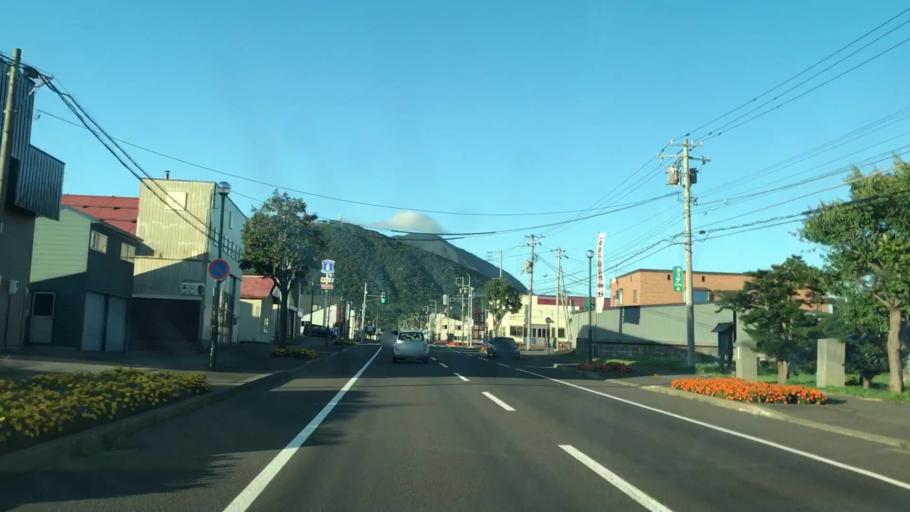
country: JP
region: Hokkaido
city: Niseko Town
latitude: 42.7332
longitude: 140.8730
